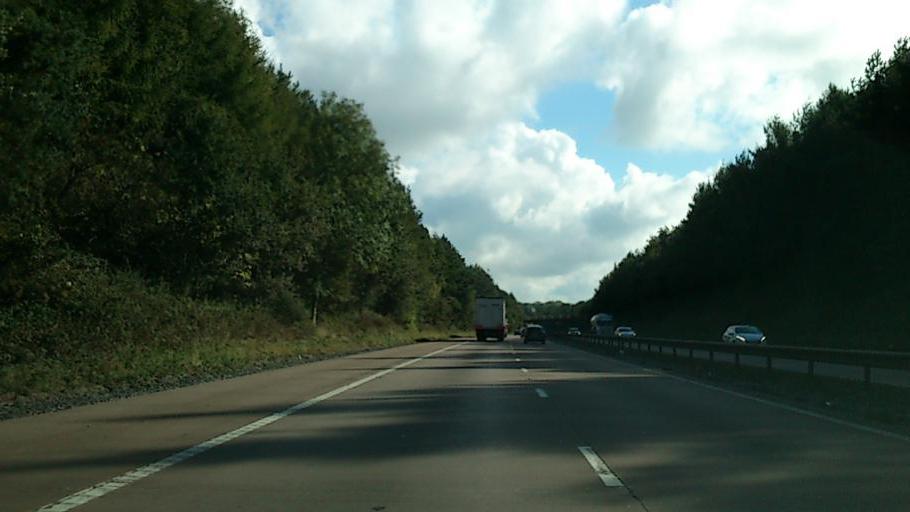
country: GB
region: England
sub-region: Staffordshire
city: Codsall
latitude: 52.6481
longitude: -2.2309
